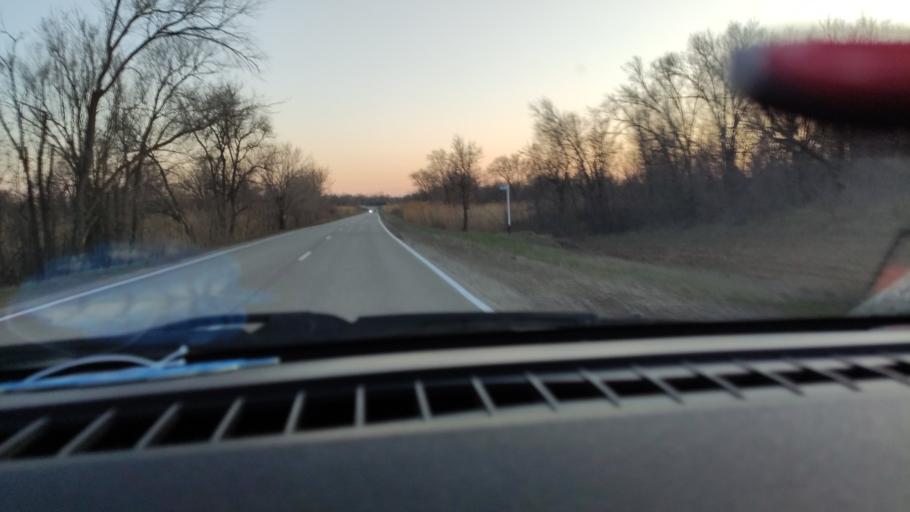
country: RU
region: Saratov
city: Privolzhskiy
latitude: 51.2353
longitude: 45.9222
